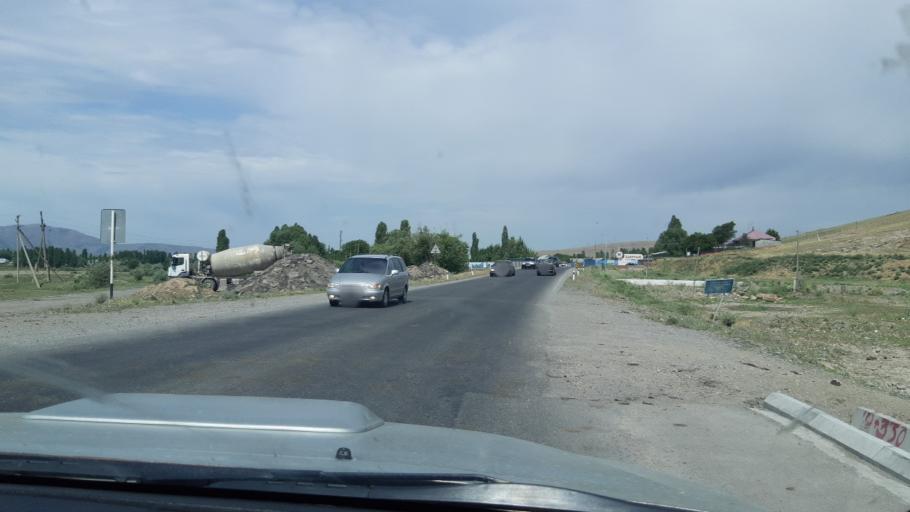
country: KZ
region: Ongtustik Qazaqstan
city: Turar Ryskulov
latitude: 42.5495
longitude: 70.3017
